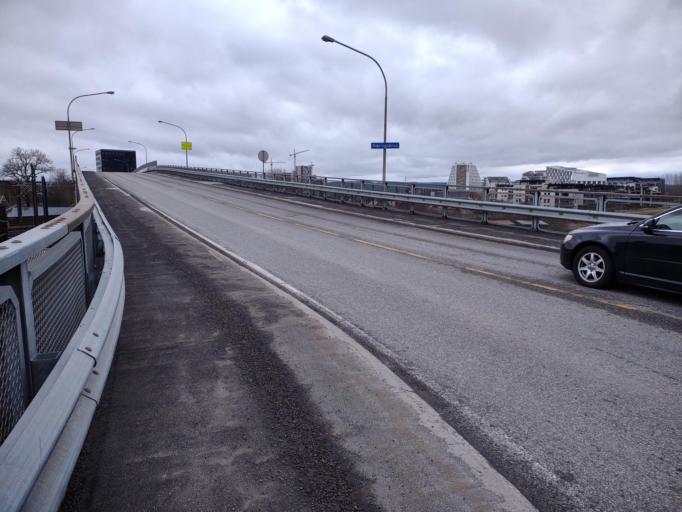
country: NO
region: Akershus
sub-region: Skedsmo
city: Lillestrom
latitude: 59.9515
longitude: 11.0369
